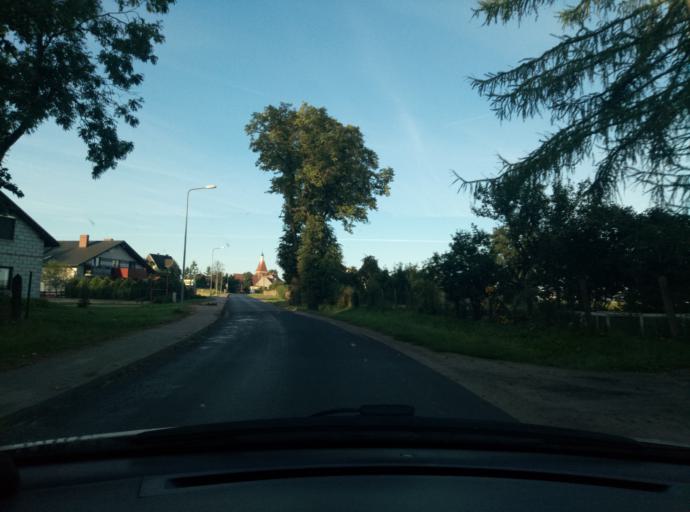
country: PL
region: Kujawsko-Pomorskie
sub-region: Powiat brodnicki
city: Jablonowo Pomorskie
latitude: 53.3979
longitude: 19.1603
